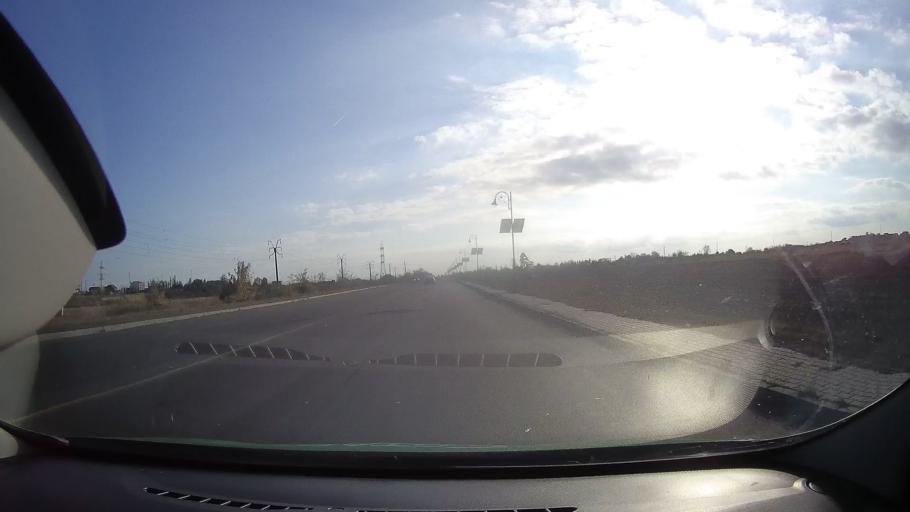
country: RO
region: Constanta
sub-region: Comuna Navodari
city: Navodari
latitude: 44.3049
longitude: 28.6149
